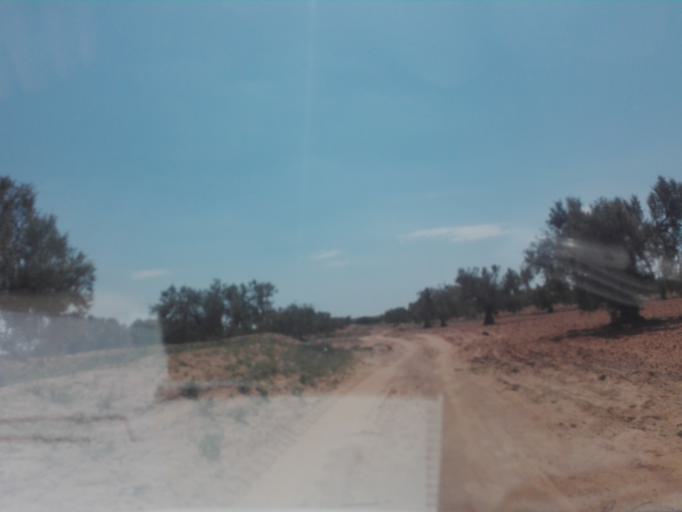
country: TN
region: Safaqis
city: Bi'r `Ali Bin Khalifah
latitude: 34.6101
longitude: 10.3535
